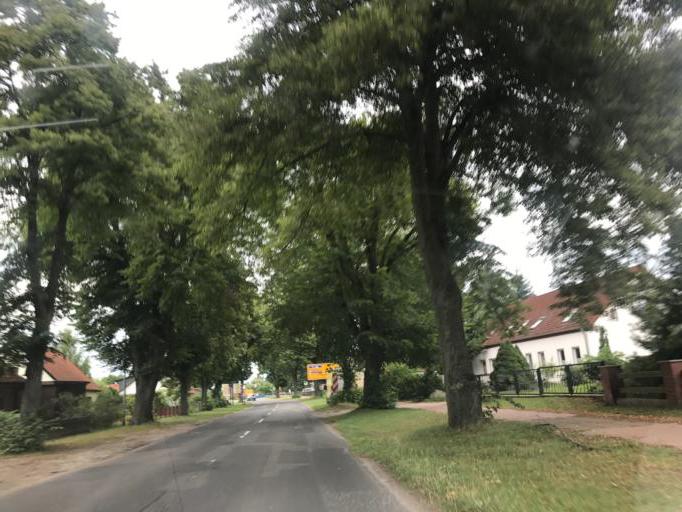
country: DE
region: Mecklenburg-Vorpommern
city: Rechlin
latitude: 53.2708
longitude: 12.7998
